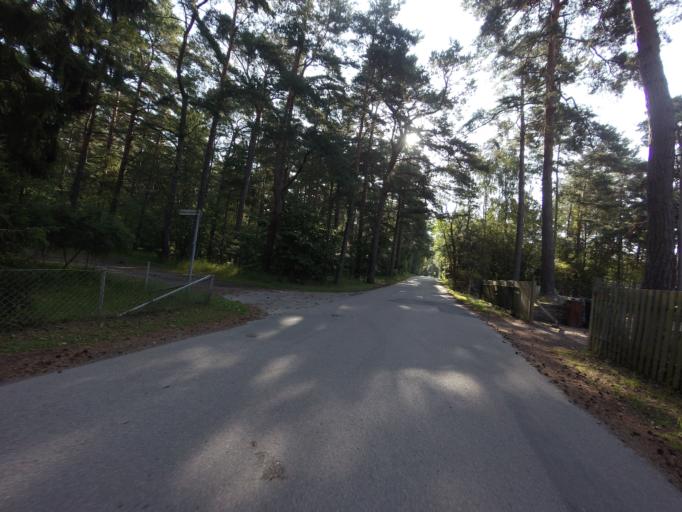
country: SE
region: Skane
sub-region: Landskrona
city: Asmundtorp
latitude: 55.8324
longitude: 12.9374
